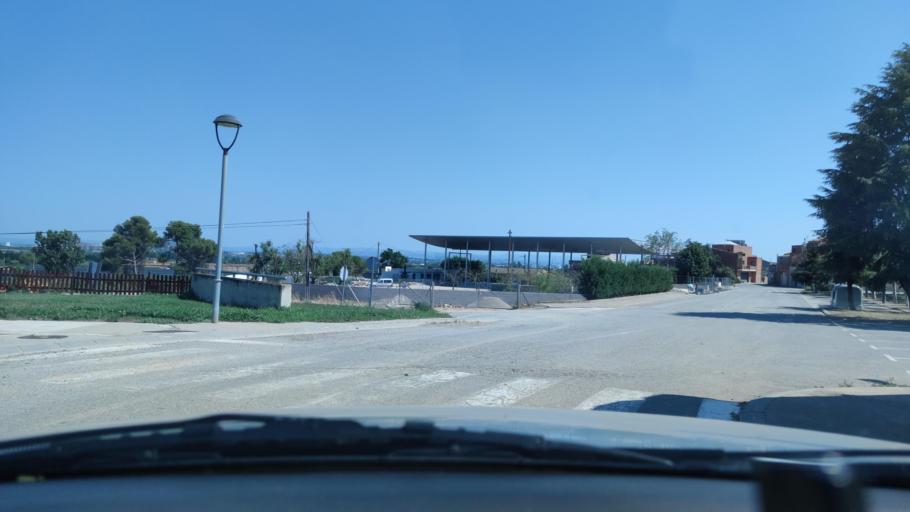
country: ES
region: Catalonia
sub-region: Provincia de Lleida
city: Torrefarrera
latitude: 41.6747
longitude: 0.6311
